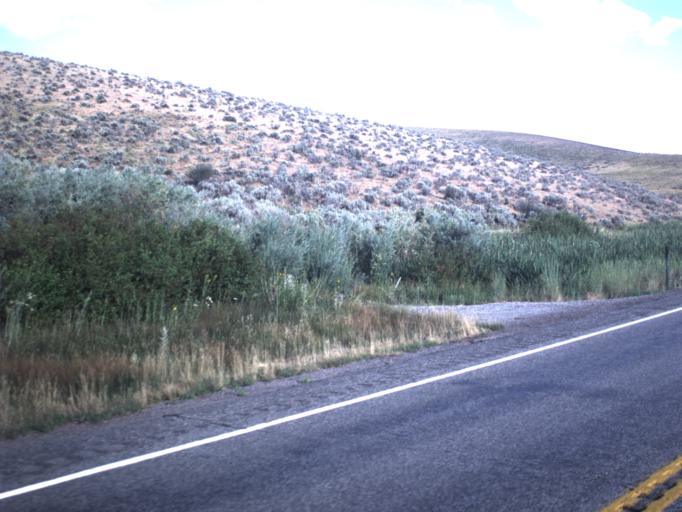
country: US
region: Utah
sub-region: Sanpete County
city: Fairview
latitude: 39.8263
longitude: -111.5106
